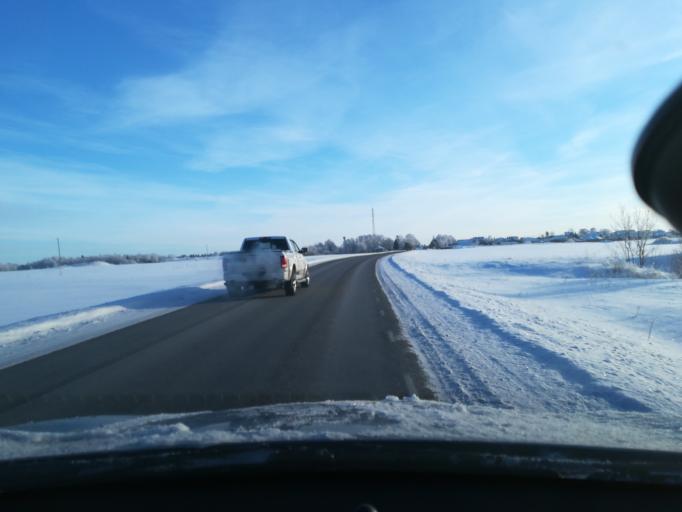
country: EE
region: Harju
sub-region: Harku vald
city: Tabasalu
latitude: 59.3675
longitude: 24.4811
